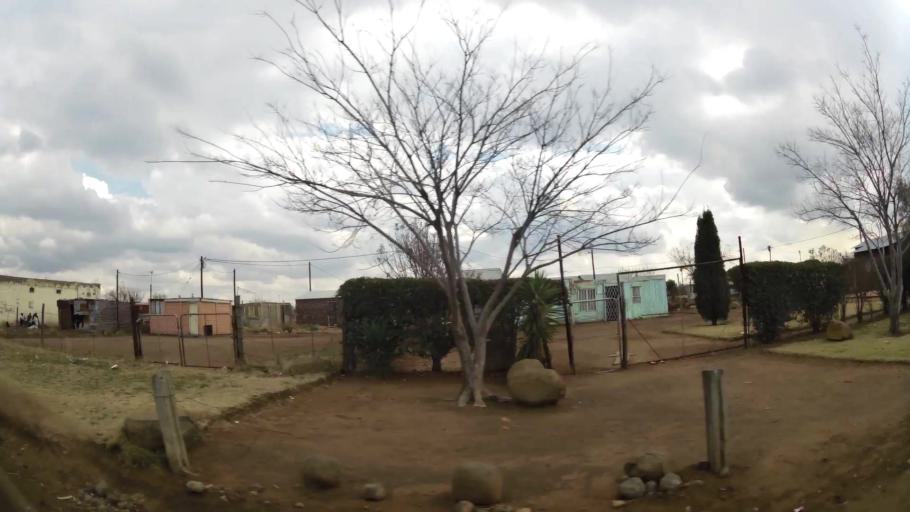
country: ZA
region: Orange Free State
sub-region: Fezile Dabi District Municipality
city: Sasolburg
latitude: -26.8545
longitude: 27.8924
